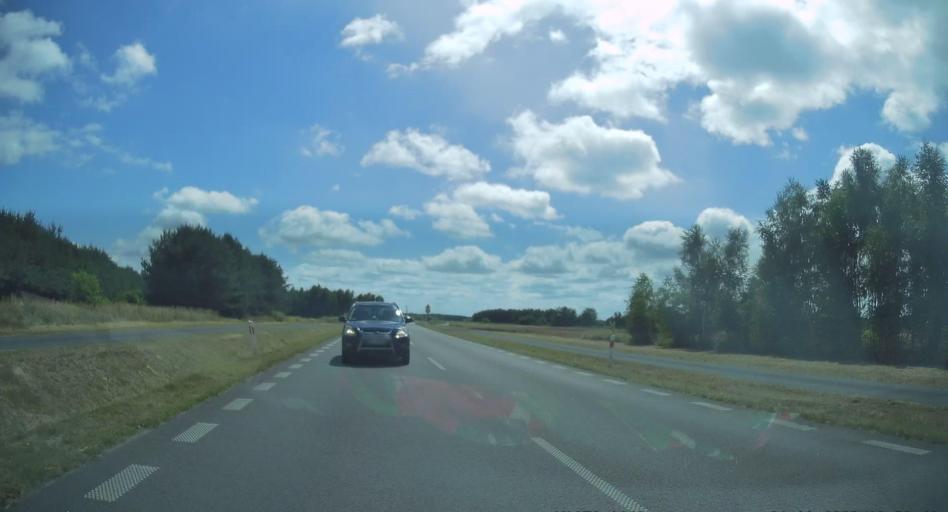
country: PL
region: Subcarpathian Voivodeship
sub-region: Powiat mielecki
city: Padew Narodowa
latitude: 50.3792
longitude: 21.4724
